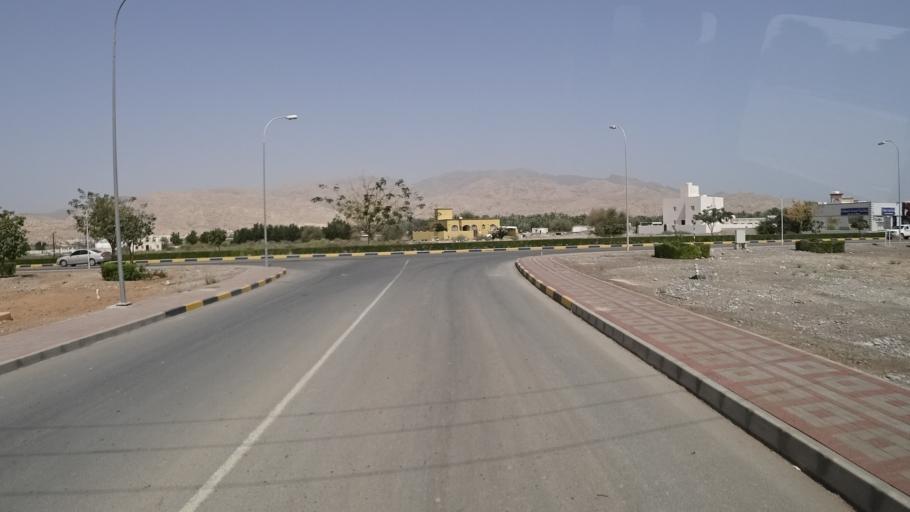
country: OM
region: Muhafazat Masqat
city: Muscat
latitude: 23.2545
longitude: 58.9101
